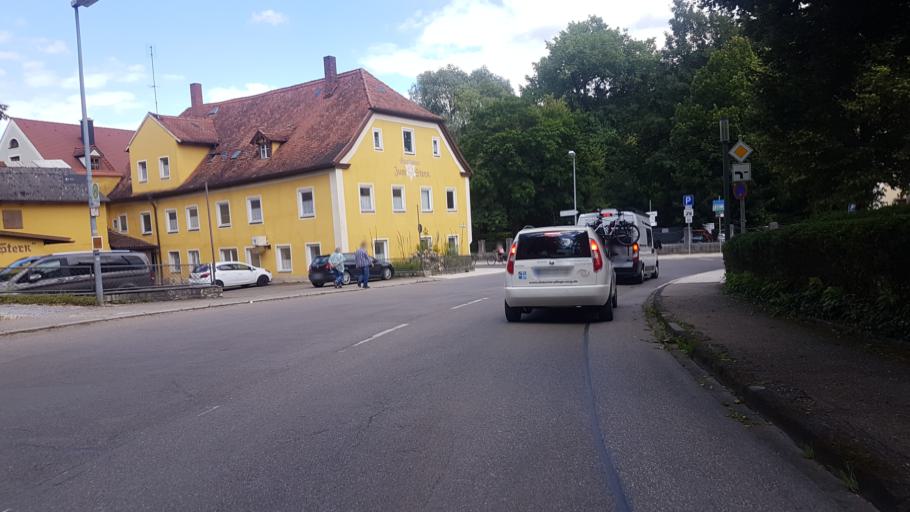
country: DE
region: Bavaria
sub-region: Regierungsbezirk Mittelfranken
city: Pappenheim
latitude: 48.9322
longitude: 10.9724
